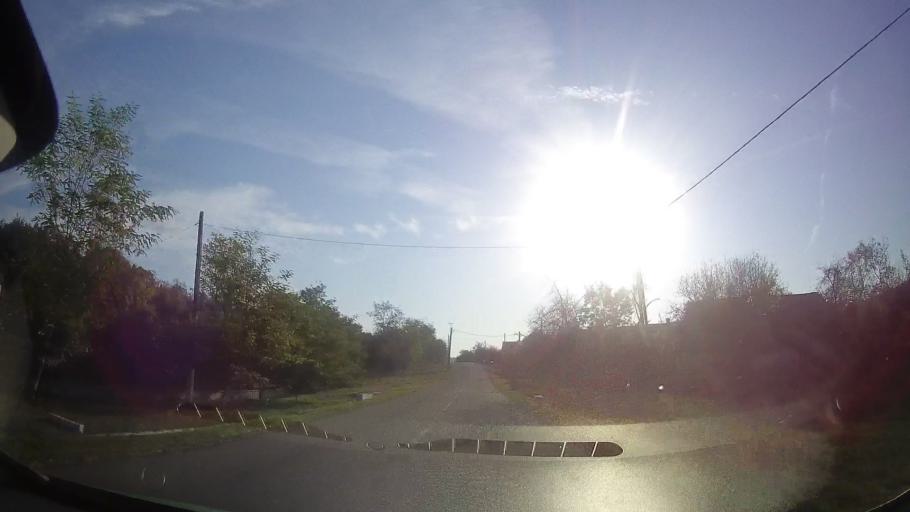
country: RO
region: Timis
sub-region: Comuna Bogda
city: Bogda
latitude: 45.9746
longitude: 21.5921
